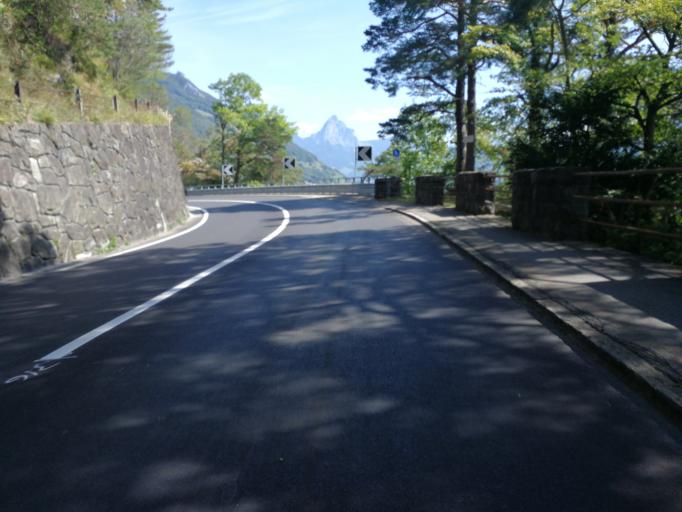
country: CH
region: Schwyz
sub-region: Bezirk Gersau
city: Gersau
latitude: 46.9928
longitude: 8.5598
